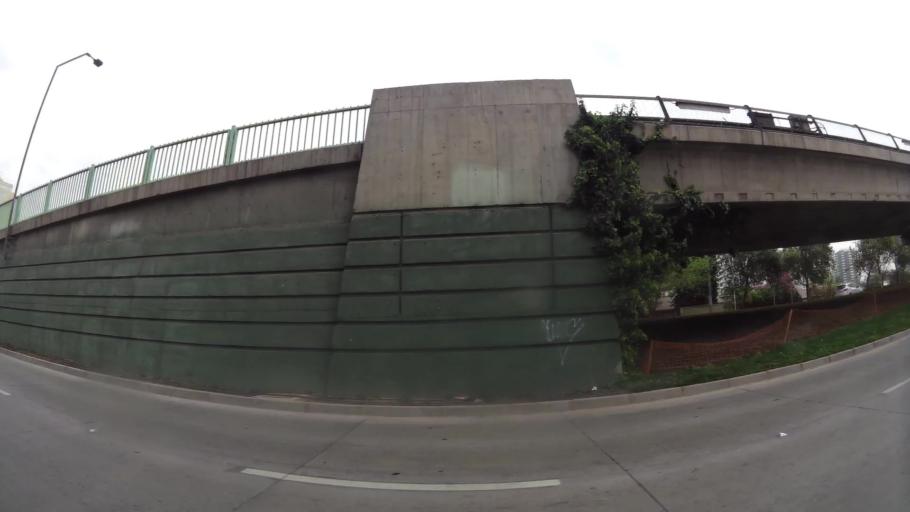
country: CL
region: Santiago Metropolitan
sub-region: Provincia de Santiago
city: Villa Presidente Frei, Nunoa, Santiago, Chile
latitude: -33.5161
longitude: -70.6024
